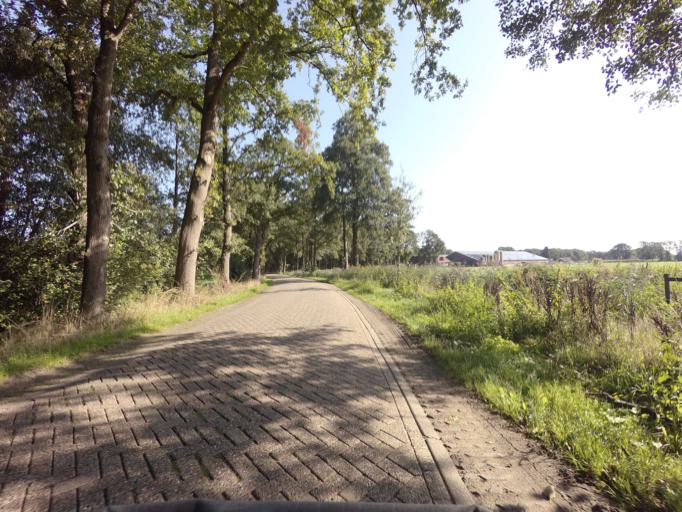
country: NL
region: Overijssel
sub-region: Gemeente Raalte
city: Raalte
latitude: 52.4253
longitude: 6.2971
